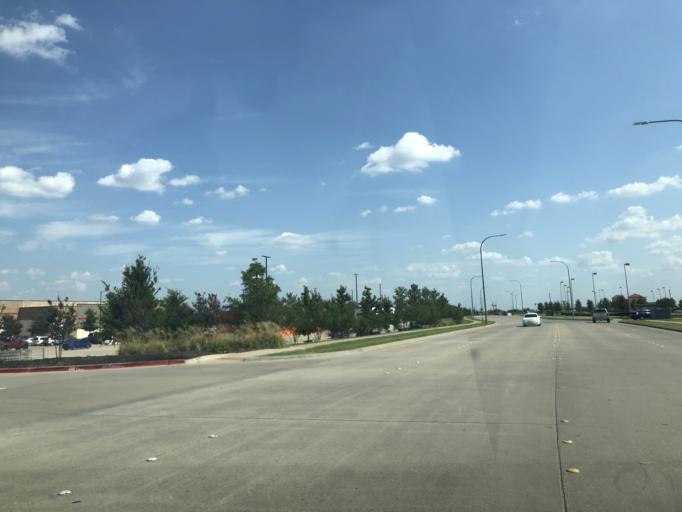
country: US
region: Texas
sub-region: Tarrant County
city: Blue Mound
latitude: 32.9021
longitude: -97.3221
